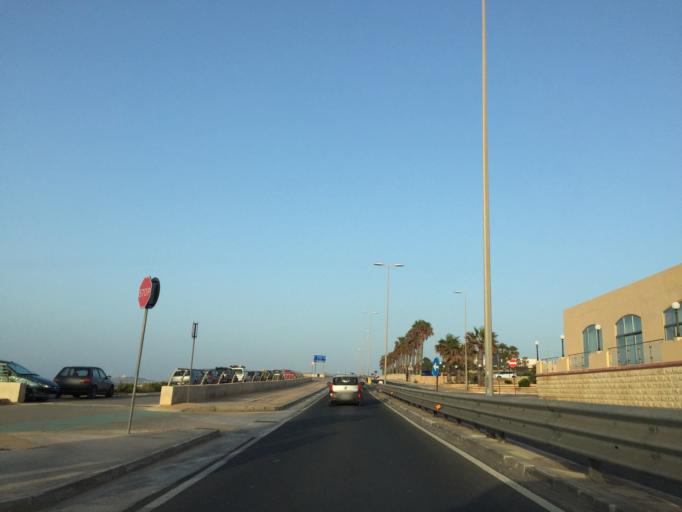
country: MT
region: Il-Mellieha
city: Mellieha
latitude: 35.9867
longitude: 14.3321
